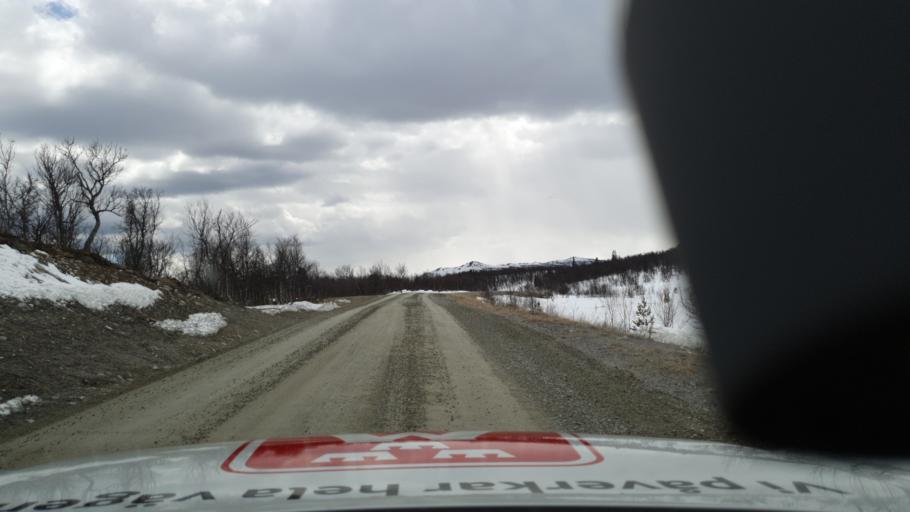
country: SE
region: Jaemtland
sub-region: Are Kommun
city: Are
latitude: 62.6248
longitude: 12.6322
